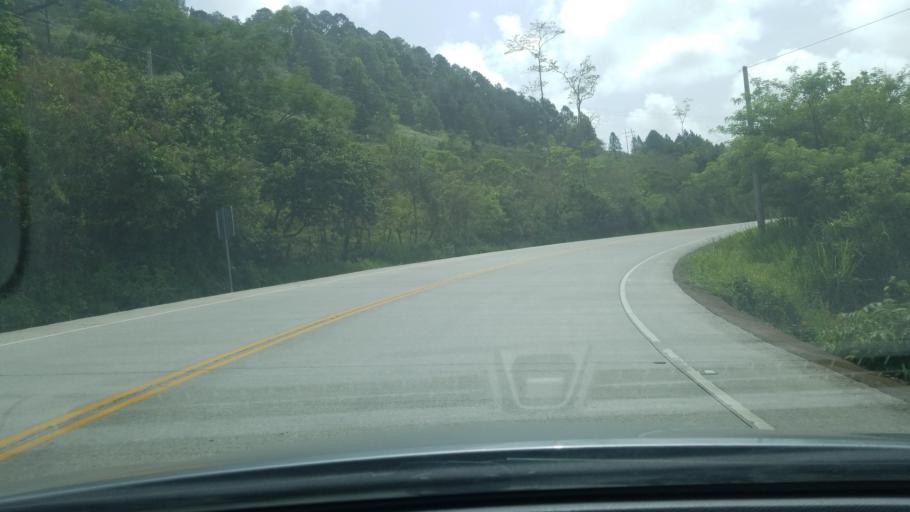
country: HN
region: Copan
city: San Jeronimo
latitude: 14.9347
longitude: -88.9310
